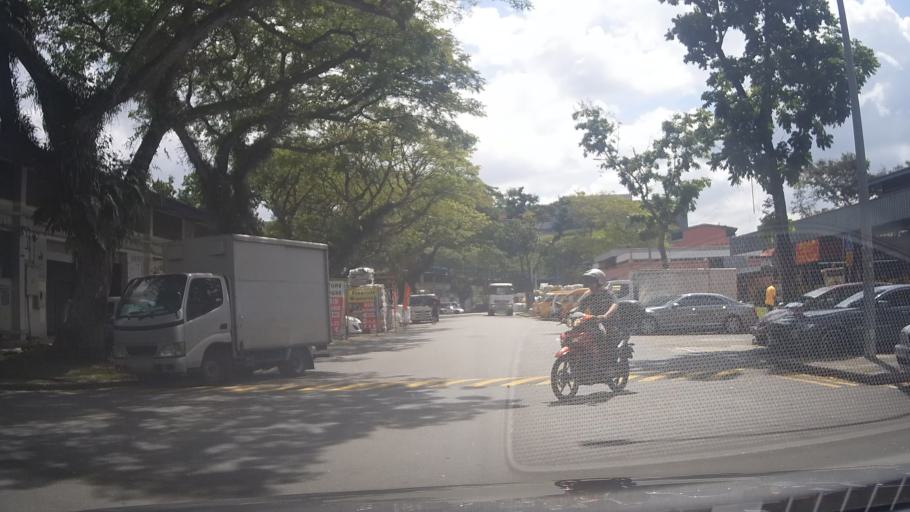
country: MY
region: Johor
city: Johor Bahru
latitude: 1.4413
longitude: 103.7811
